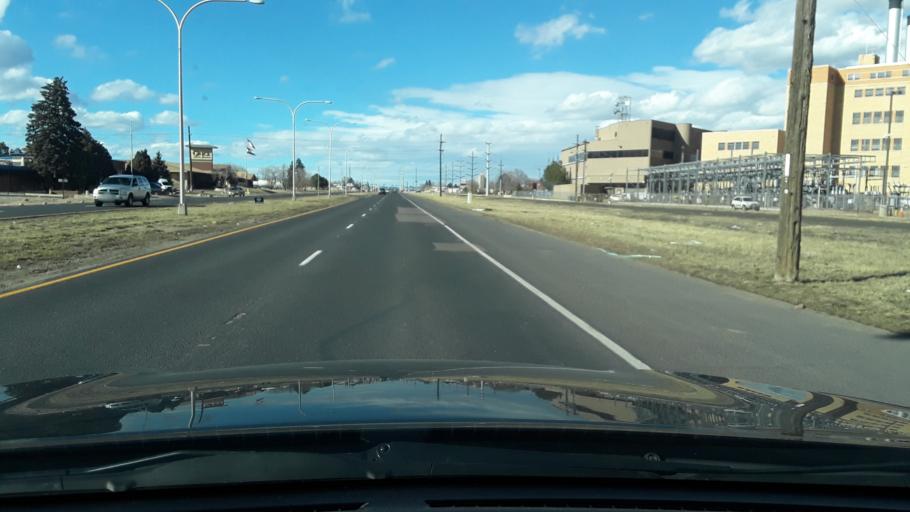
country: US
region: Colorado
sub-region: El Paso County
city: Colorado Springs
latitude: 38.8798
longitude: -104.8186
